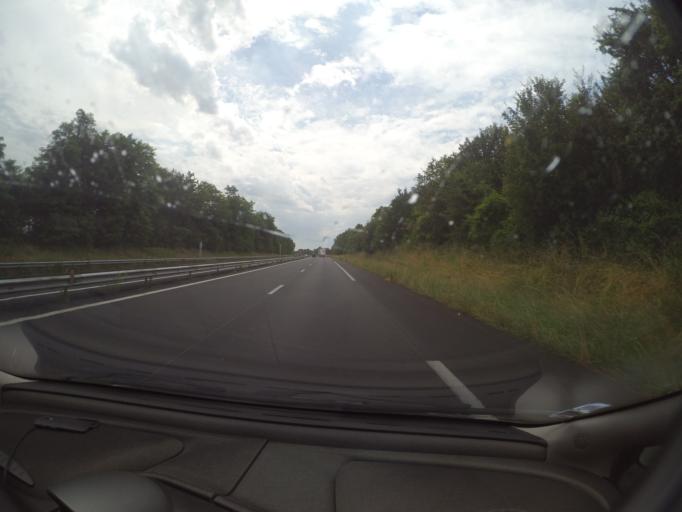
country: FR
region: Pays de la Loire
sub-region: Departement de Maine-et-Loire
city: Seiches-sur-le-Loir
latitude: 47.5863
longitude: -0.3280
